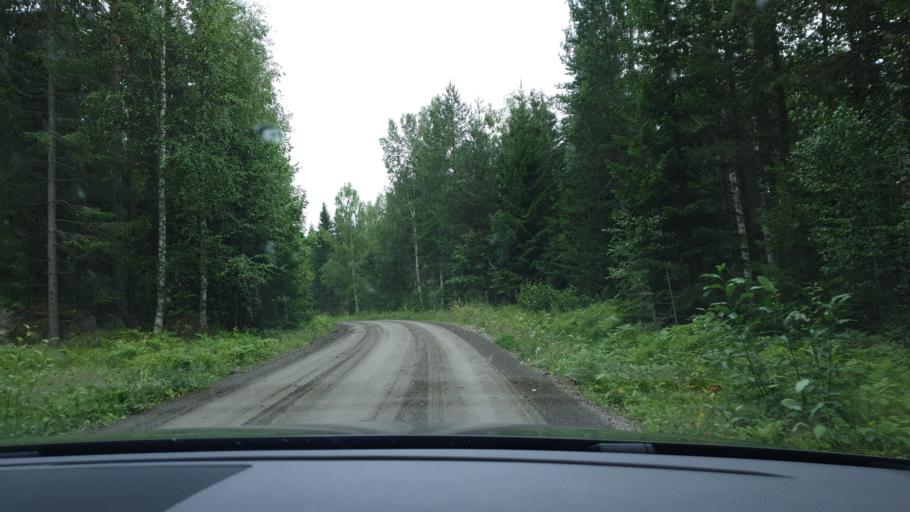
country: SE
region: Gaevleborg
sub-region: Hudiksvalls Kommun
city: Iggesund
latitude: 61.5245
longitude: 17.0147
